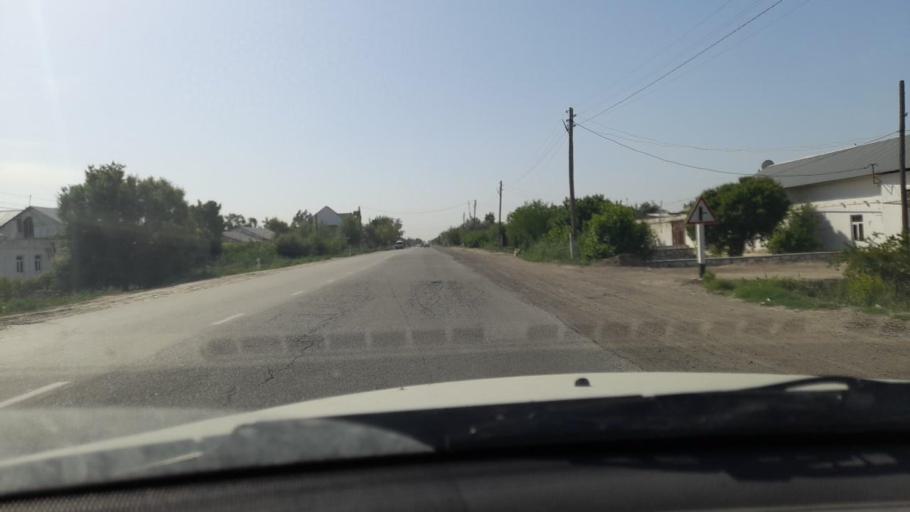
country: UZ
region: Bukhara
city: Romiton
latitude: 39.9033
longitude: 64.4038
